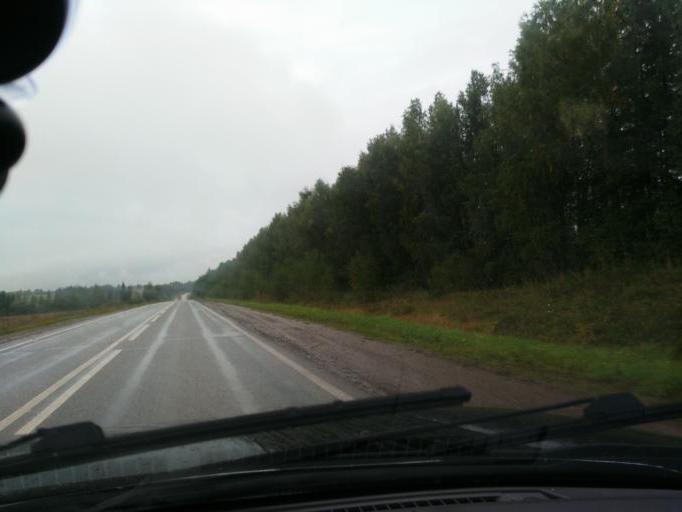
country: RU
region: Perm
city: Osa
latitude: 57.3791
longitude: 55.6094
